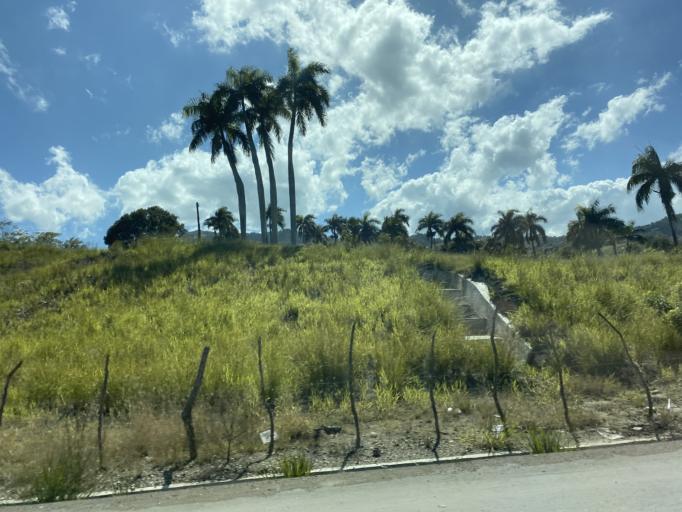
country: DO
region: Puerto Plata
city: Imbert
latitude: 19.7943
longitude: -70.8015
